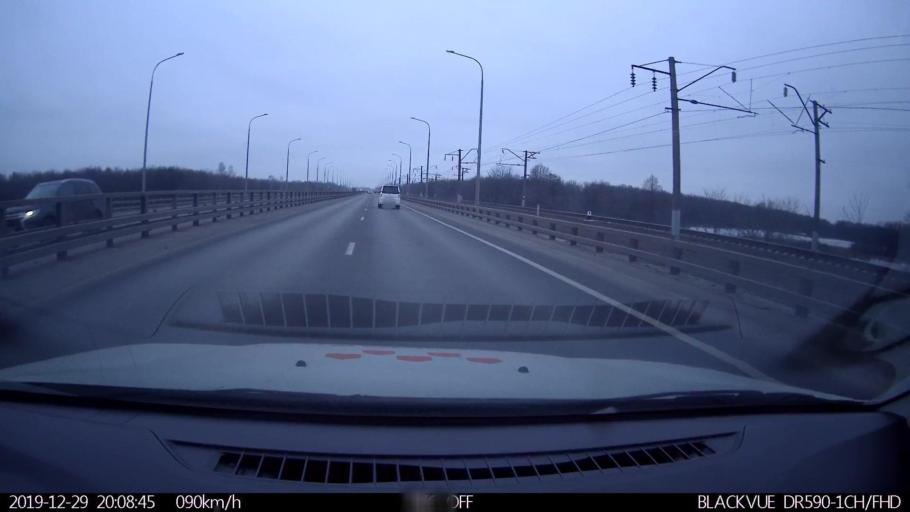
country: RU
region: Nizjnij Novgorod
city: Neklyudovo
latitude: 56.3819
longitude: 43.9601
